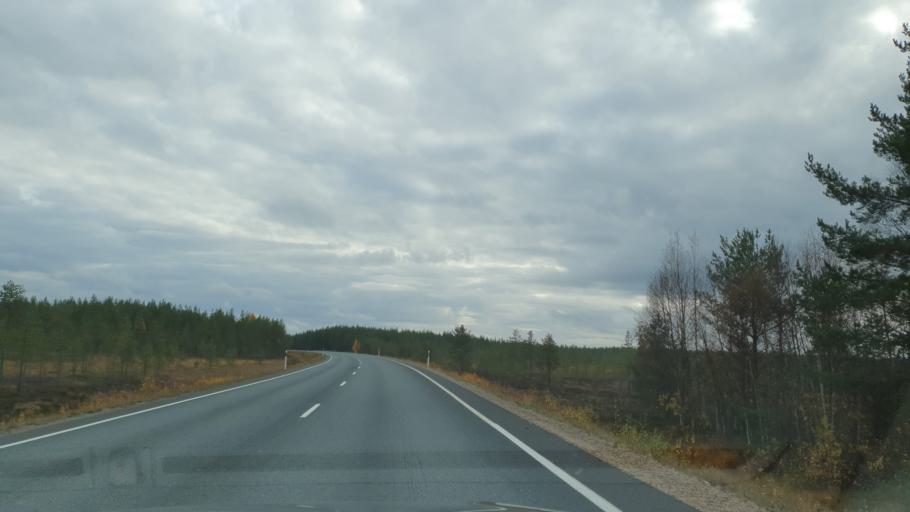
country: FI
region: Northern Ostrobothnia
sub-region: Oulunkaari
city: Pudasjaervi
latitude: 65.4027
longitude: 26.9065
